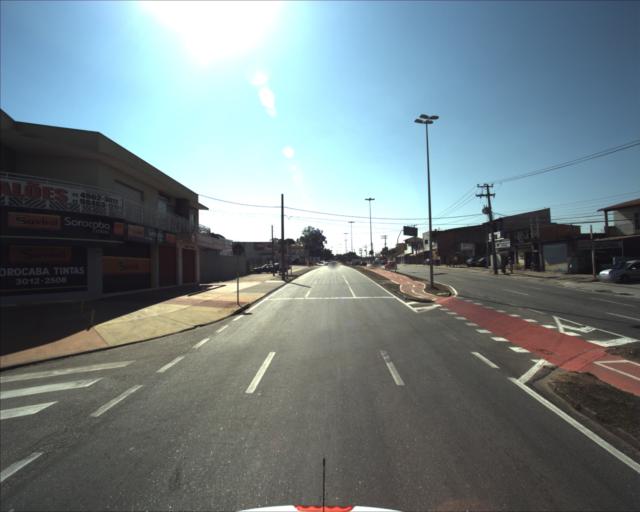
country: BR
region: Sao Paulo
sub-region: Sorocaba
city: Sorocaba
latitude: -23.4405
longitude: -47.4785
